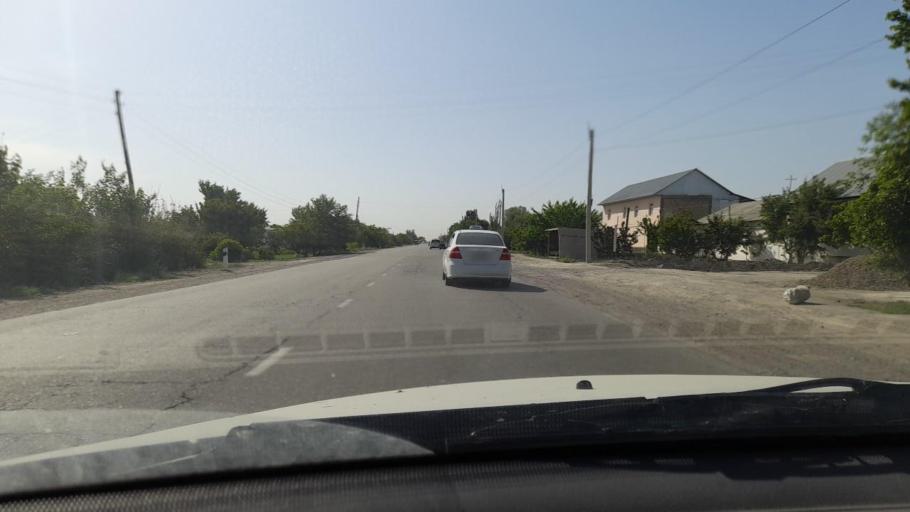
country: UZ
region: Bukhara
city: Romiton
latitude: 39.9082
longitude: 64.3985
